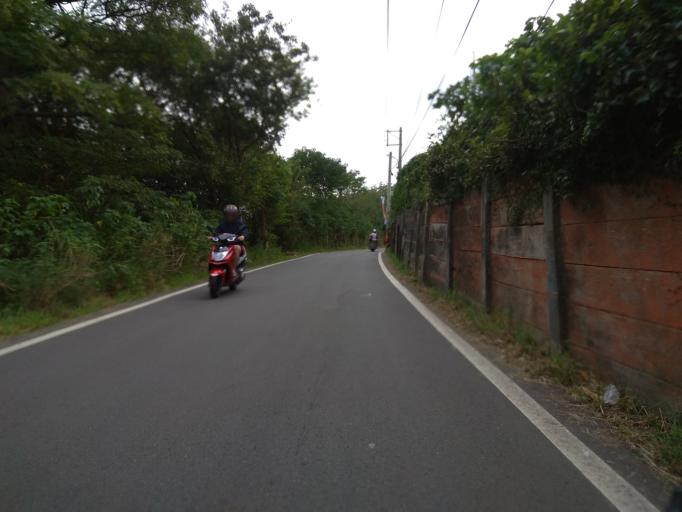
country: TW
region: Taiwan
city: Daxi
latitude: 24.9349
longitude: 121.2050
